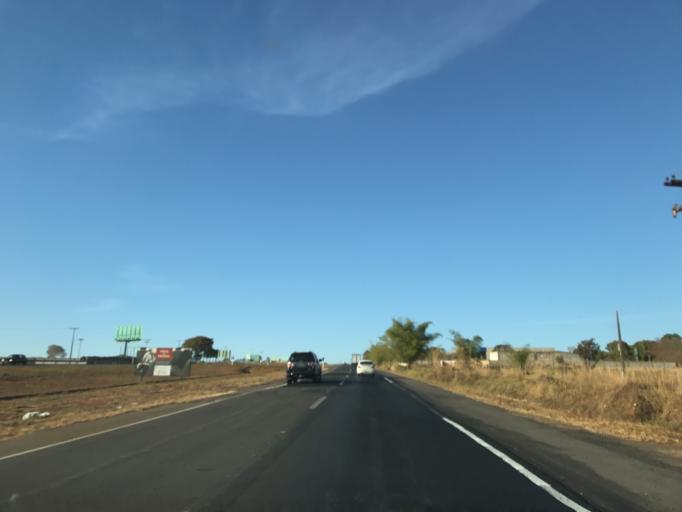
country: BR
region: Goias
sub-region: Aparecida De Goiania
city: Aparecida de Goiania
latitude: -16.8739
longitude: -49.2519
